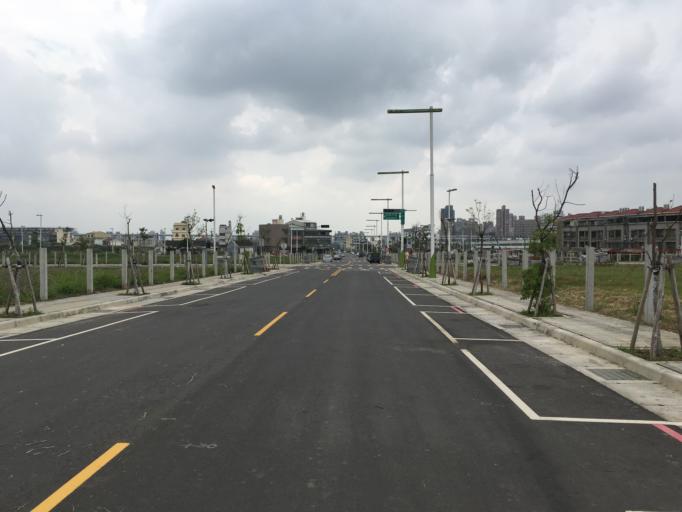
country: TW
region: Taiwan
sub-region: Taichung City
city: Taichung
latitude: 24.1884
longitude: 120.7050
